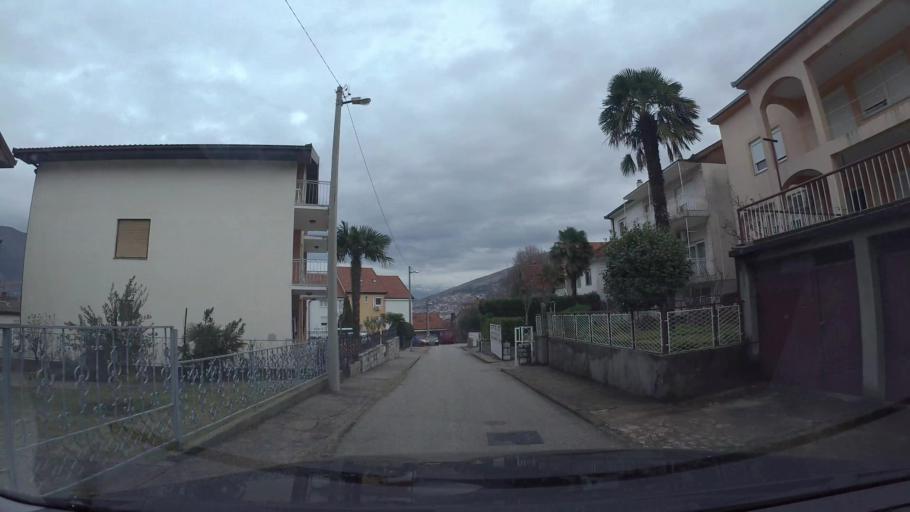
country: BA
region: Federation of Bosnia and Herzegovina
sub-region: Hercegovacko-Bosanski Kanton
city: Mostar
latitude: 43.3360
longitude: 17.8001
